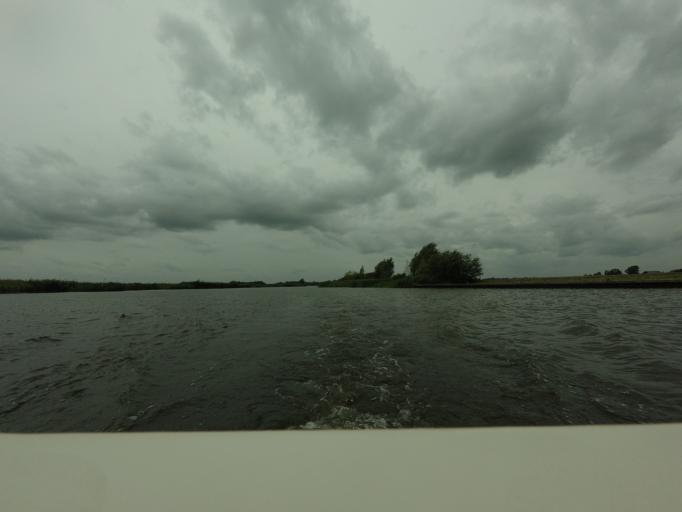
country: NL
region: Friesland
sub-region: Gemeente Boarnsterhim
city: Aldeboarn
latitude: 53.0987
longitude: 5.9185
